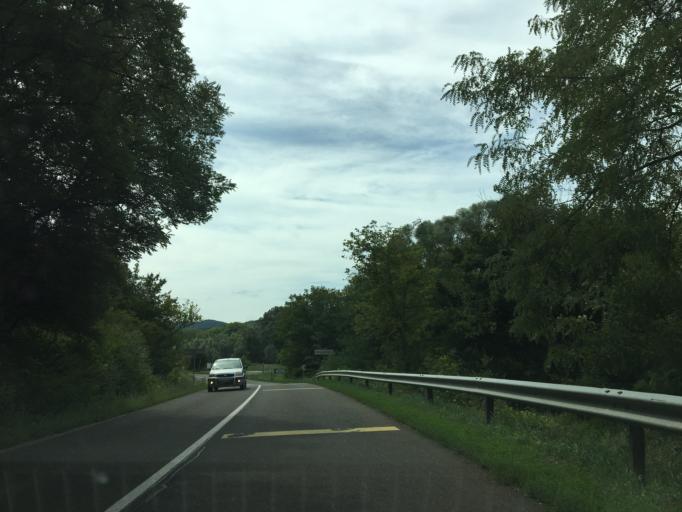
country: HU
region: Pest
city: Szob
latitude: 47.8472
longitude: 18.8230
